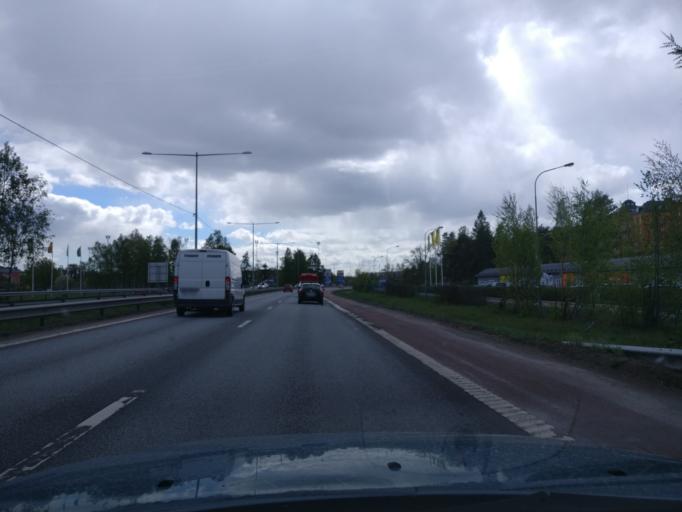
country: SE
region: Vaermland
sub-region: Karlstads Kommun
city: Karlstad
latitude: 59.3892
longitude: 13.4936
